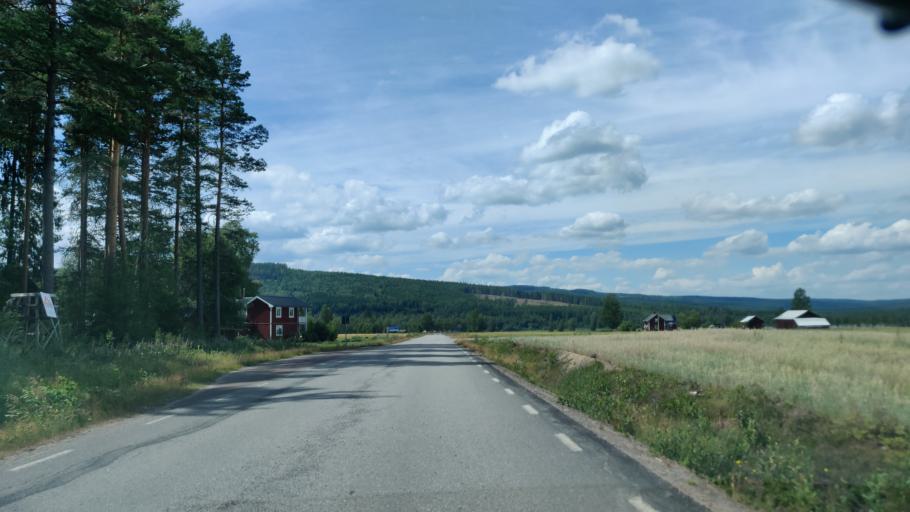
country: SE
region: Vaermland
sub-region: Hagfors Kommun
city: Ekshaerad
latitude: 60.0714
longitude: 13.4954
